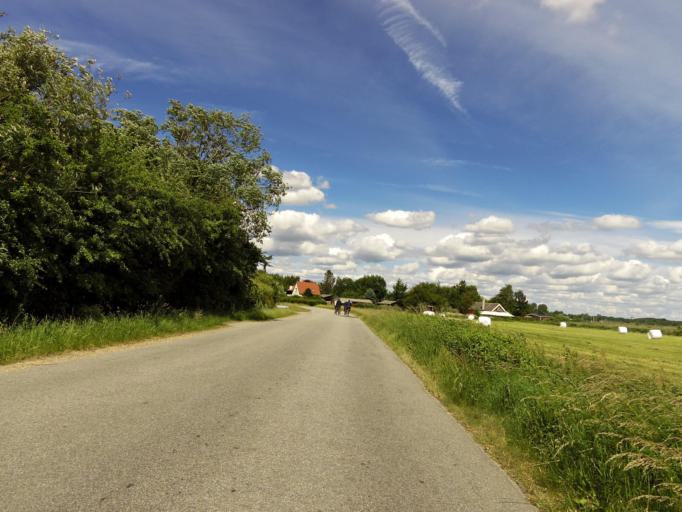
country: DK
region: South Denmark
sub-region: Esbjerg Kommune
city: Ribe
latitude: 55.3162
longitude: 8.7611
